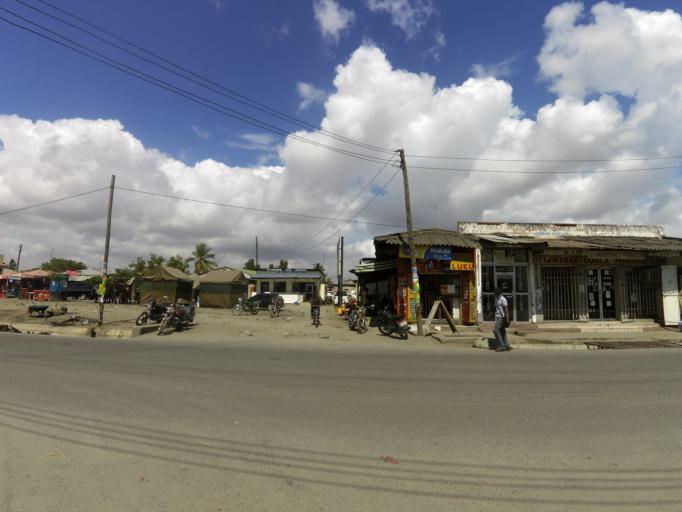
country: TZ
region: Dar es Salaam
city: Magomeni
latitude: -6.7884
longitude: 39.2533
